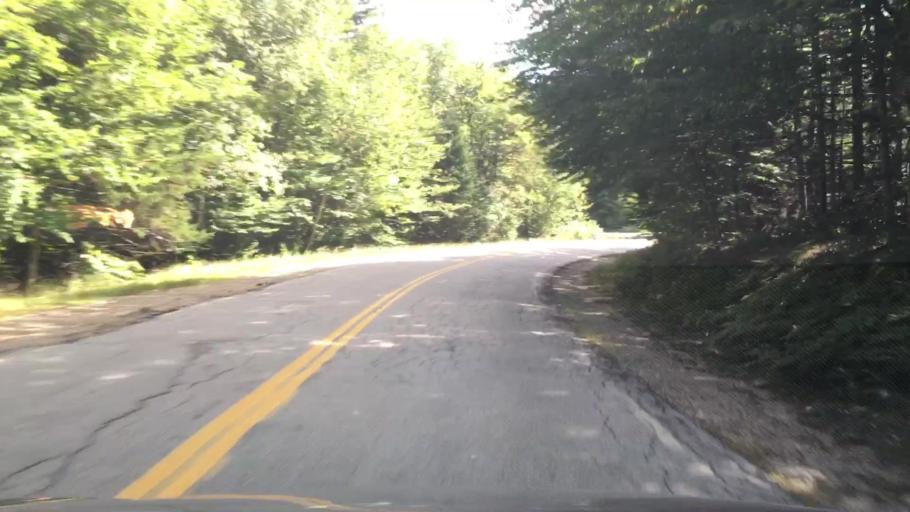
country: US
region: New Hampshire
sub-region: Carroll County
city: Tamworth
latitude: 43.9983
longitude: -71.3224
